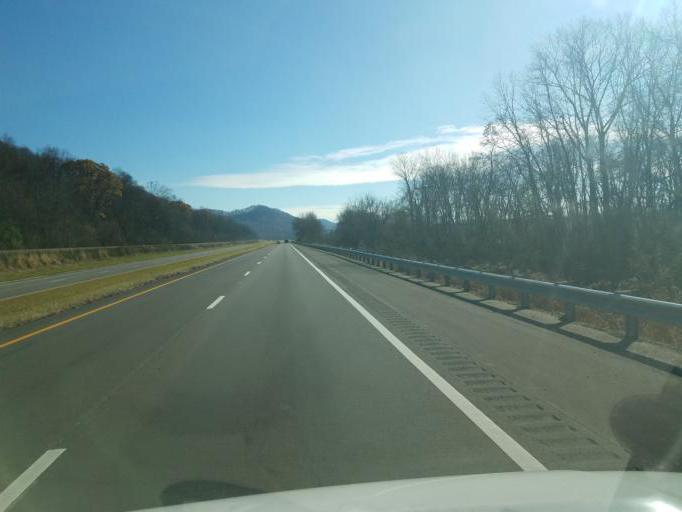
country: US
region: Ohio
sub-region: Scioto County
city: Lucasville
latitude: 38.8692
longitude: -82.9938
